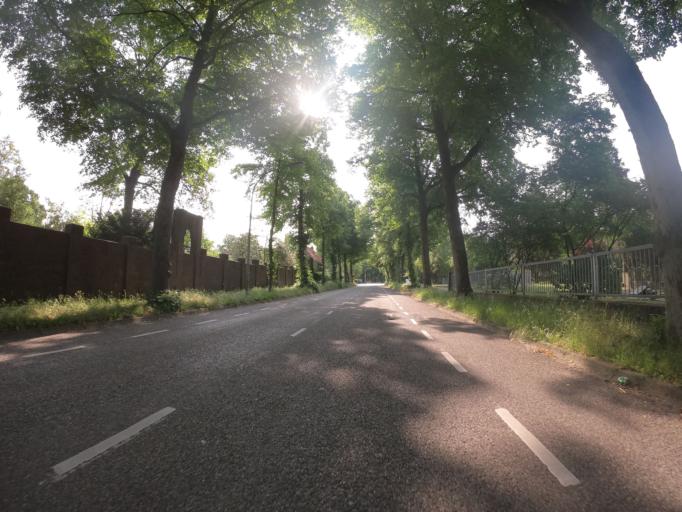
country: NL
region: Gelderland
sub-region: Gemeente Nijmegen
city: Nijmegen
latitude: 51.8308
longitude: 5.8825
